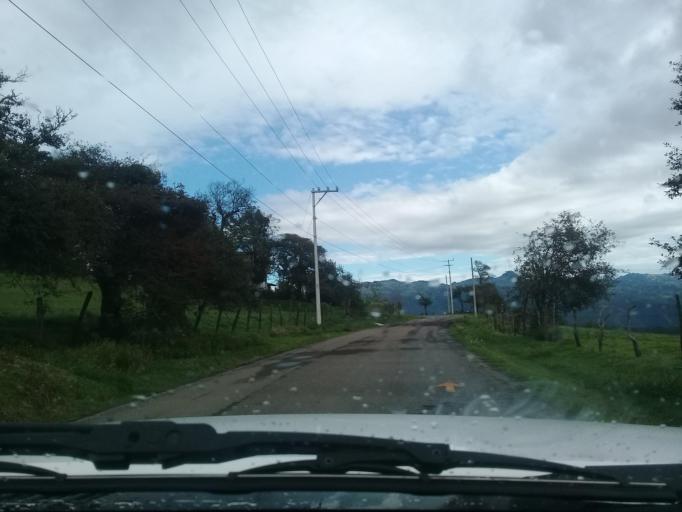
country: MX
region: Veracruz
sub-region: Acajete
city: La Joya
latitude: 19.6099
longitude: -97.0042
